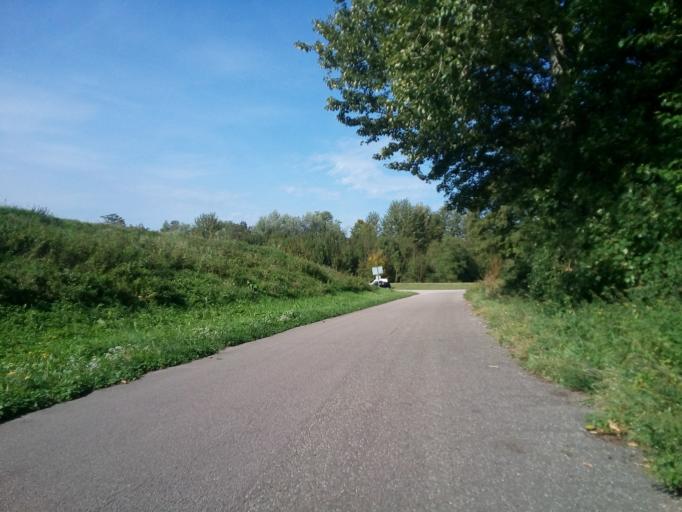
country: FR
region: Alsace
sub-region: Departement du Bas-Rhin
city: Drusenheim
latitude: 48.7444
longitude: 7.9712
